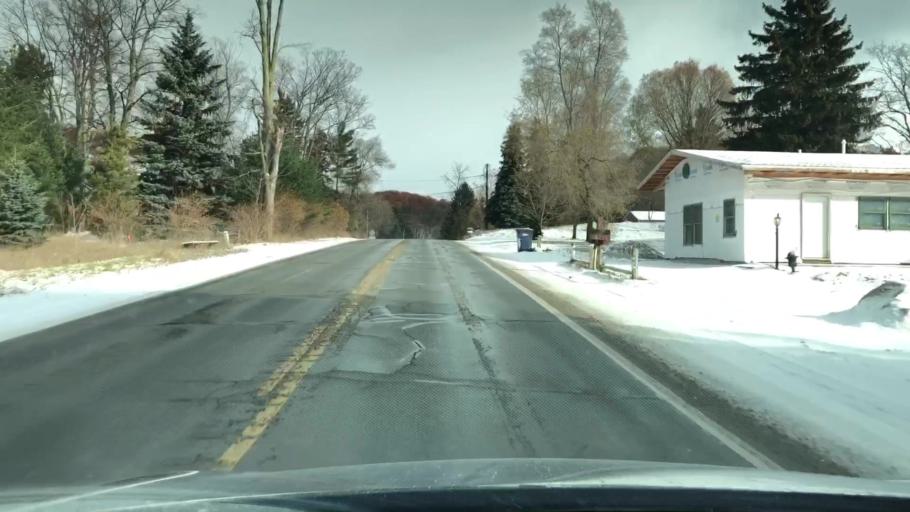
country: US
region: Michigan
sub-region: Grand Traverse County
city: Traverse City
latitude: 44.8389
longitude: -85.5353
